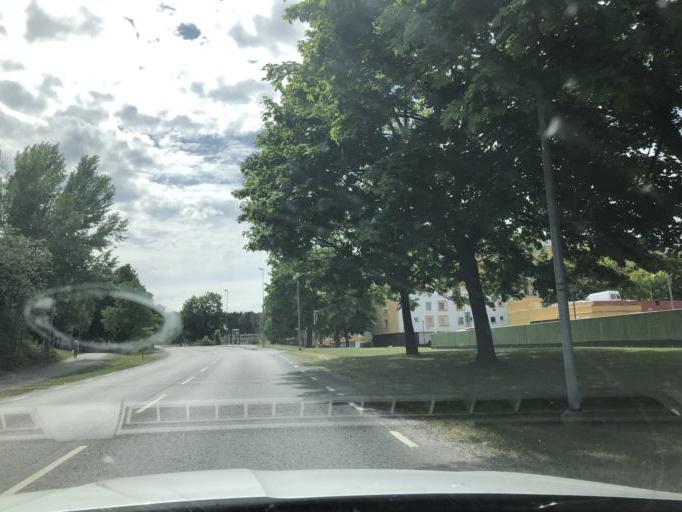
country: SE
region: Stockholm
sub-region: Botkyrka Kommun
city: Alby
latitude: 59.2362
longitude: 17.8517
